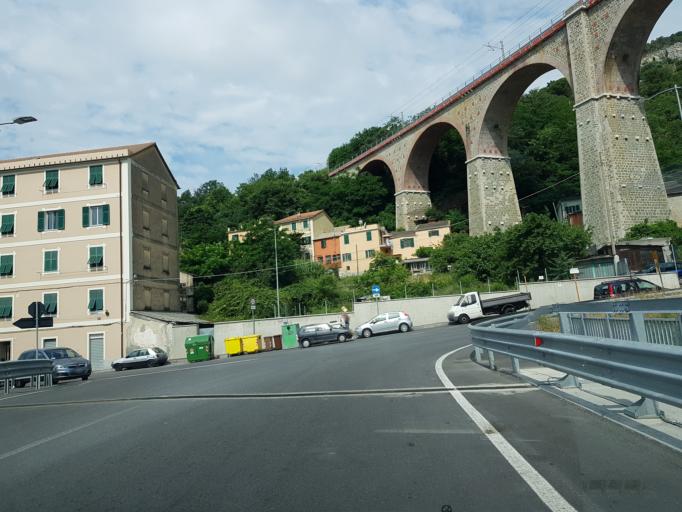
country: IT
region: Liguria
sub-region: Provincia di Genova
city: San Teodoro
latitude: 44.4350
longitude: 8.8549
